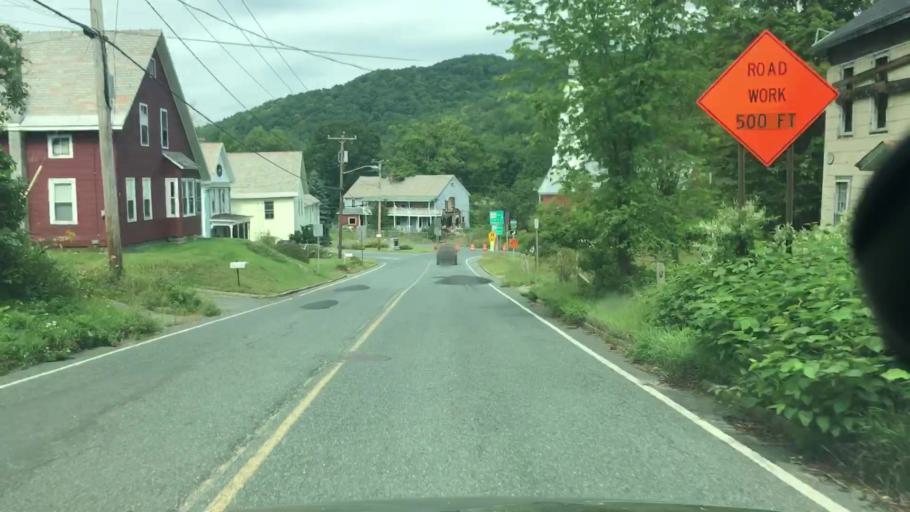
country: US
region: Massachusetts
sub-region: Franklin County
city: Colrain
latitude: 42.6721
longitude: -72.6960
